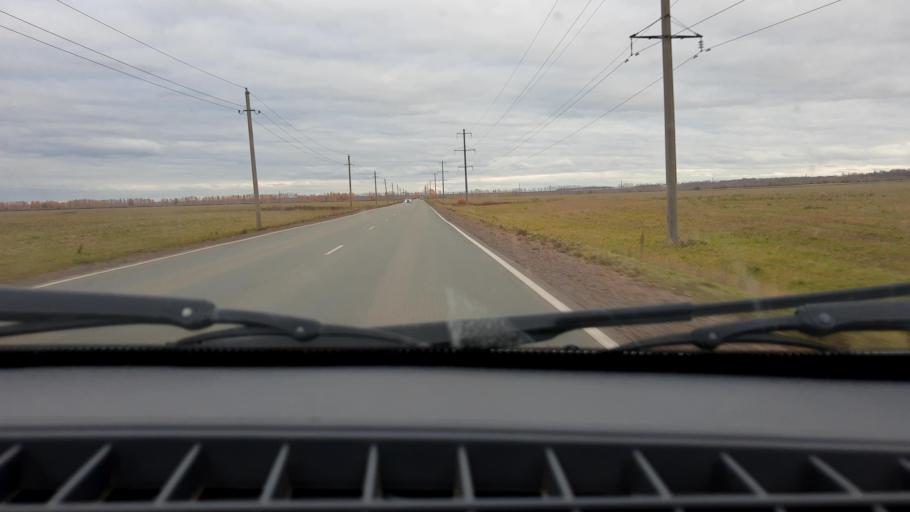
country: RU
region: Bashkortostan
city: Kabakovo
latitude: 54.5417
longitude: 56.0547
